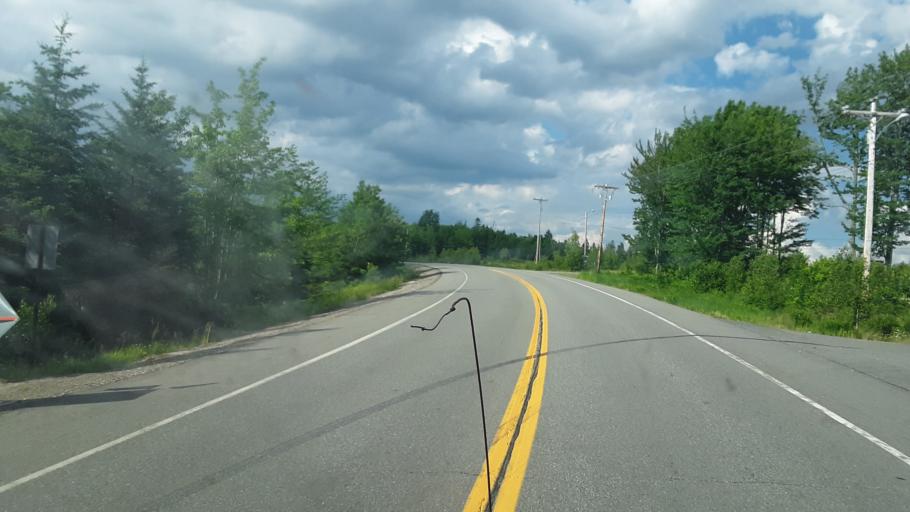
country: US
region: Maine
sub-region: Washington County
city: Machias
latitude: 45.0012
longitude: -67.5543
